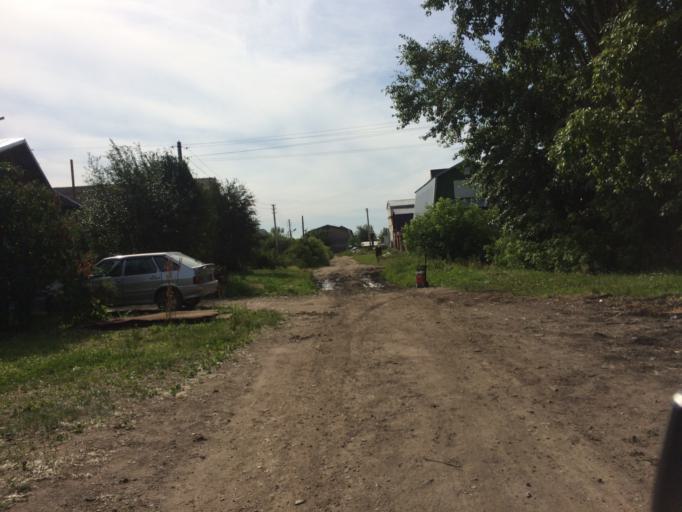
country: RU
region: Mariy-El
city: Yoshkar-Ola
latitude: 56.6514
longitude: 47.9159
